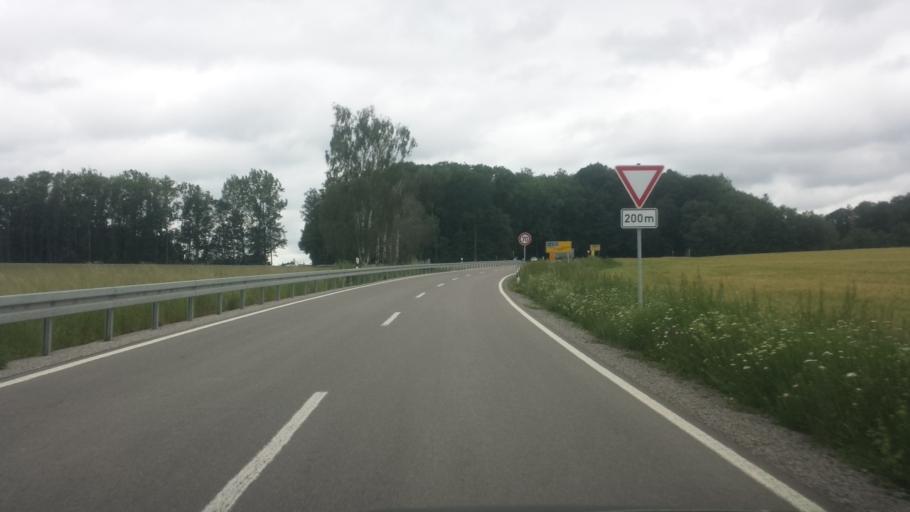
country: DE
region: Baden-Wuerttemberg
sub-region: Regierungsbezirk Stuttgart
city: Rot am See
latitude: 49.2781
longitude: 10.0110
